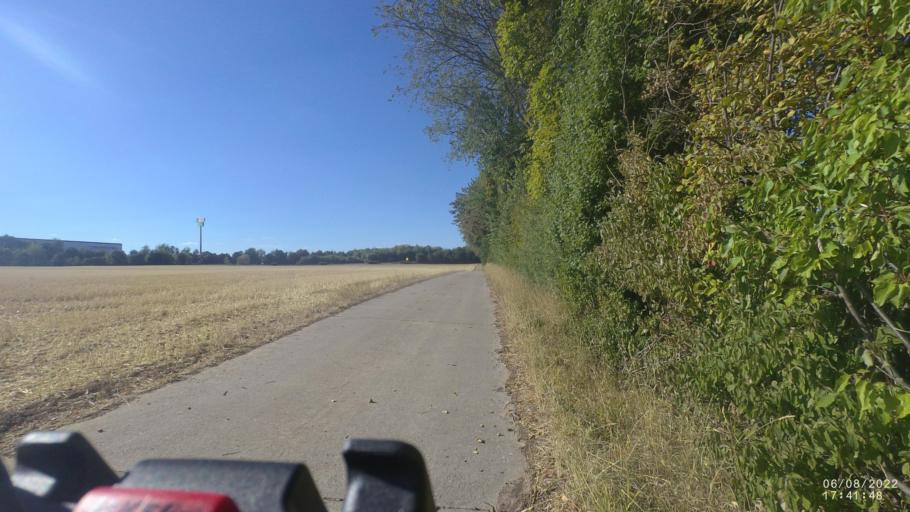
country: DE
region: Rheinland-Pfalz
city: Worrstadt
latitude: 49.8364
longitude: 8.1479
